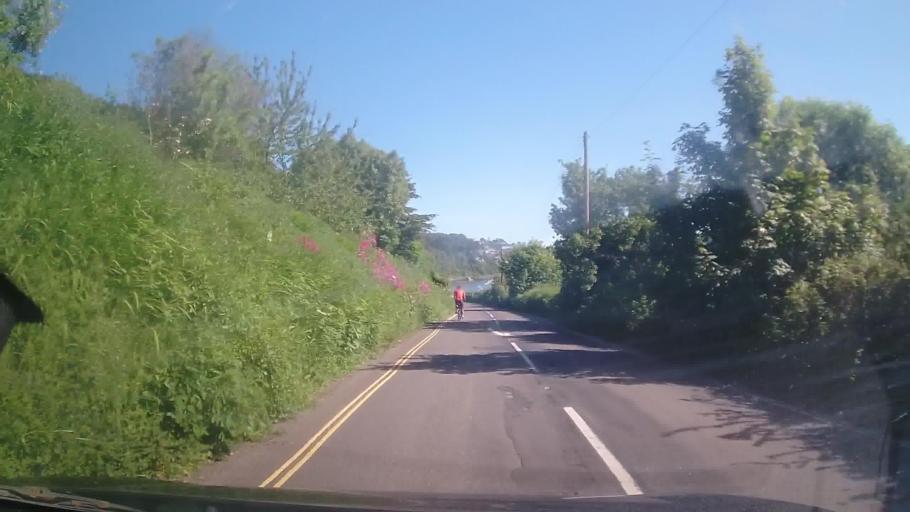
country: GB
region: England
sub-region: Devon
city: Dartmouth
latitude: 50.3625
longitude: -3.5745
